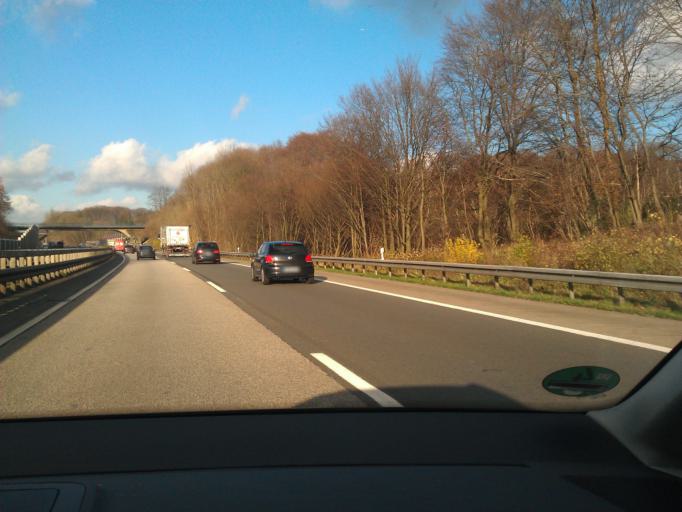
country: DE
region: North Rhine-Westphalia
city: Sprockhovel
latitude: 51.3944
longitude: 7.2642
